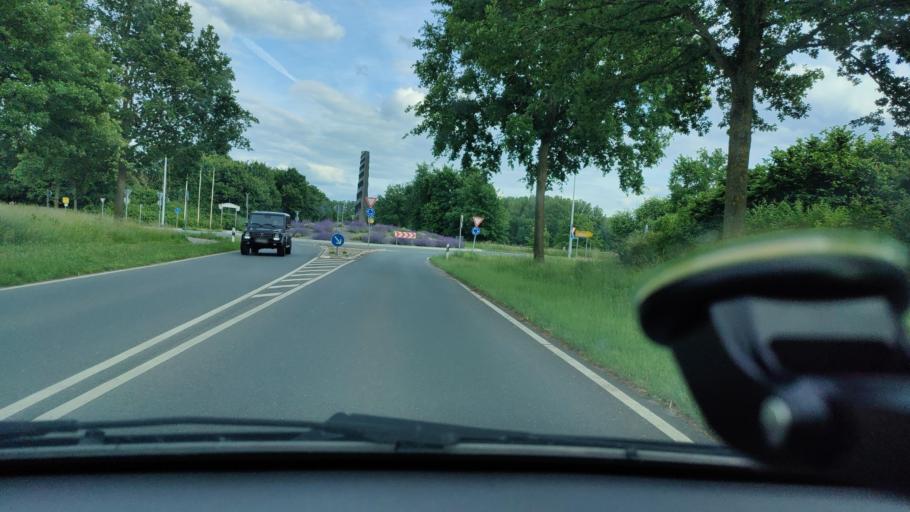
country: DE
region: North Rhine-Westphalia
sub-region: Regierungsbezirk Dusseldorf
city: Weeze
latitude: 51.6208
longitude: 6.1866
